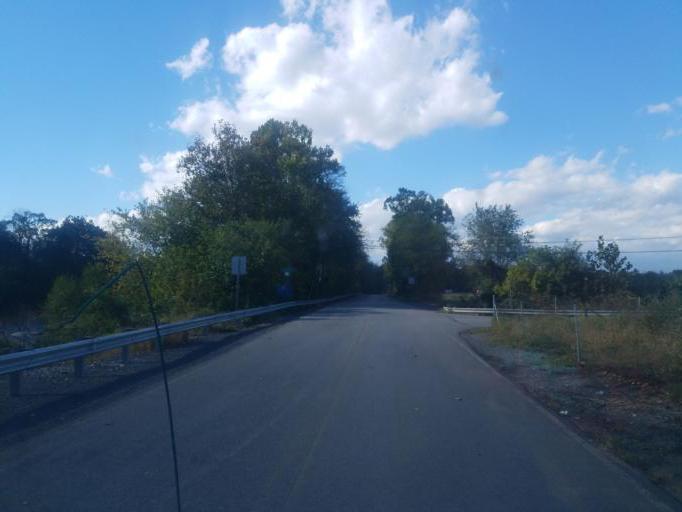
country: US
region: Pennsylvania
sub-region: Dauphin County
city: Middletown
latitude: 40.2101
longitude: -76.7165
